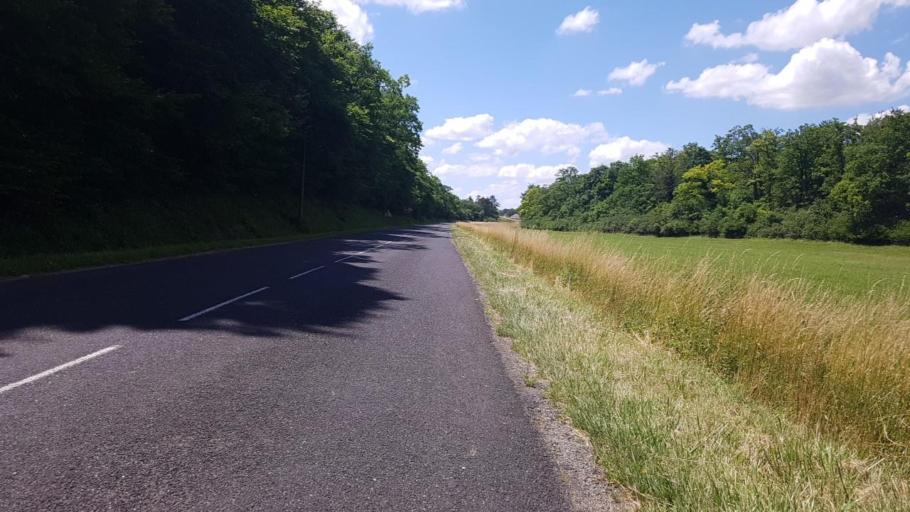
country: FR
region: Lorraine
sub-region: Departement de la Meuse
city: Vacon
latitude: 48.6697
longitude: 5.5574
